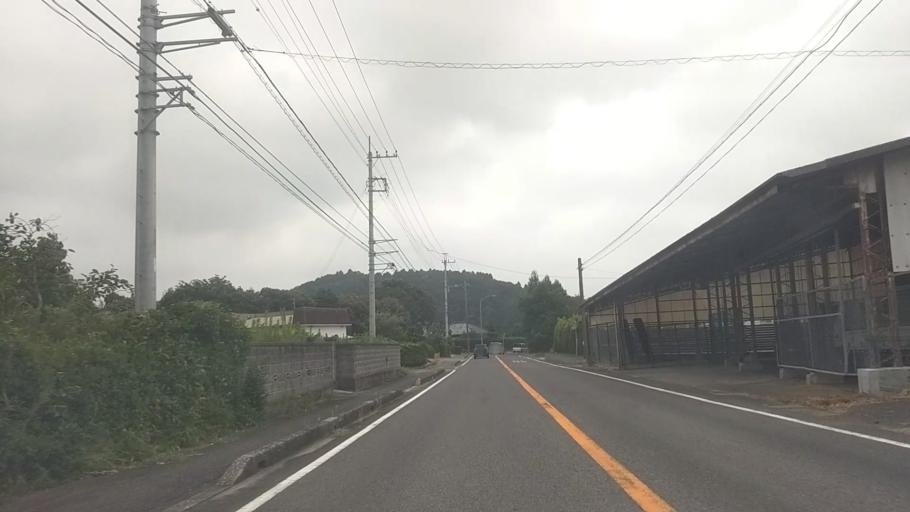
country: JP
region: Chiba
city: Ohara
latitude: 35.2638
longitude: 140.3449
